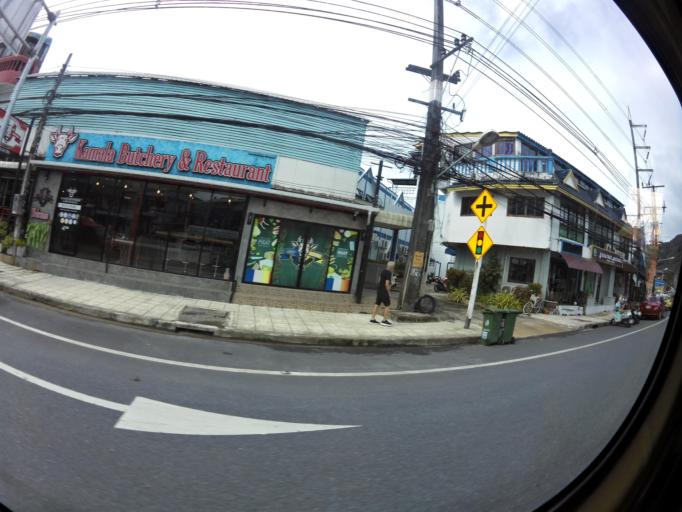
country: TH
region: Phuket
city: Patong
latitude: 7.9489
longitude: 98.2843
